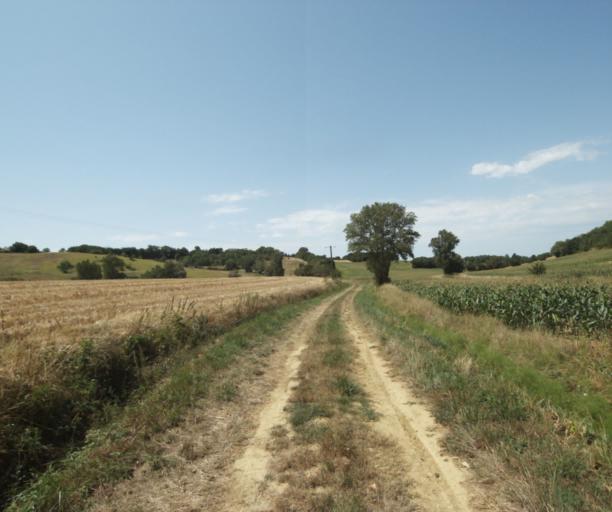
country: FR
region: Midi-Pyrenees
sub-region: Departement de la Haute-Garonne
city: Saint-Felix-Lauragais
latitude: 43.4544
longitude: 1.8638
